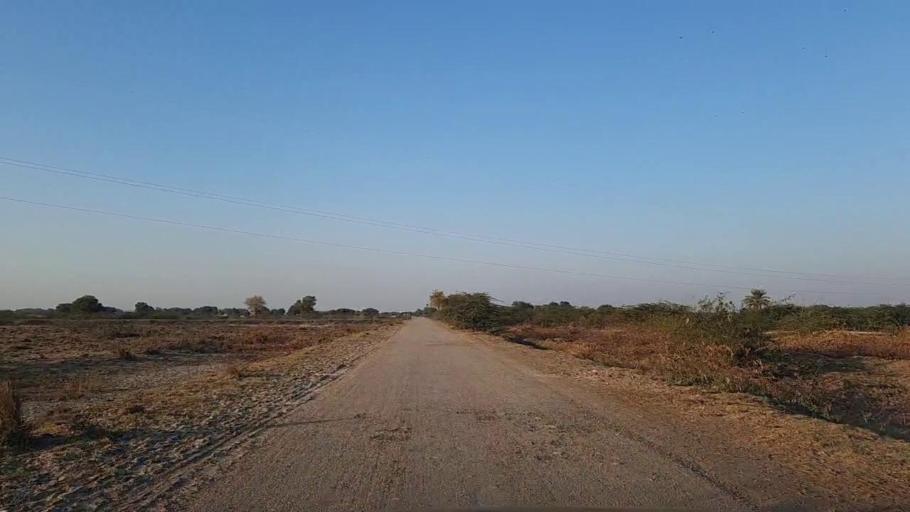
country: PK
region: Sindh
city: Nawabshah
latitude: 26.2209
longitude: 68.3379
